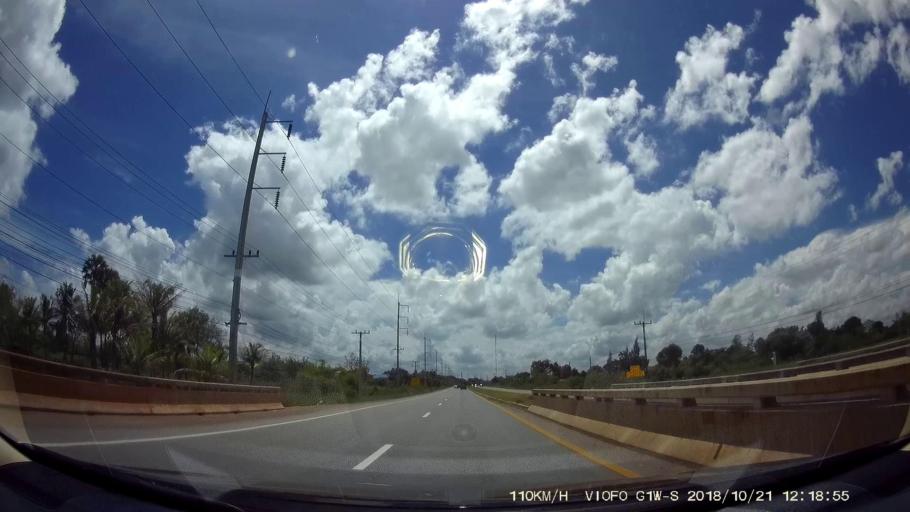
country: TH
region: Nakhon Ratchasima
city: Dan Khun Thot
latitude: 15.3089
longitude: 101.8159
